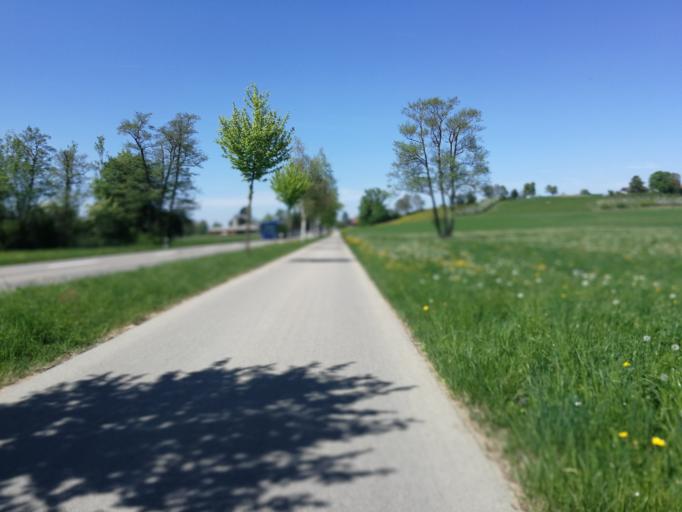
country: CH
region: Zurich
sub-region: Bezirk Uster
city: Monchaltorf
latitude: 47.3226
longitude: 8.7140
